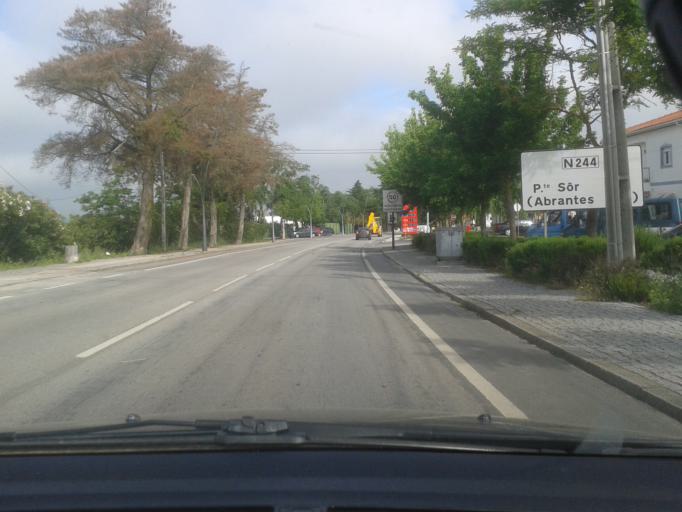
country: PT
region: Portalegre
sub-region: Avis
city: Avis
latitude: 39.0516
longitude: -7.8924
